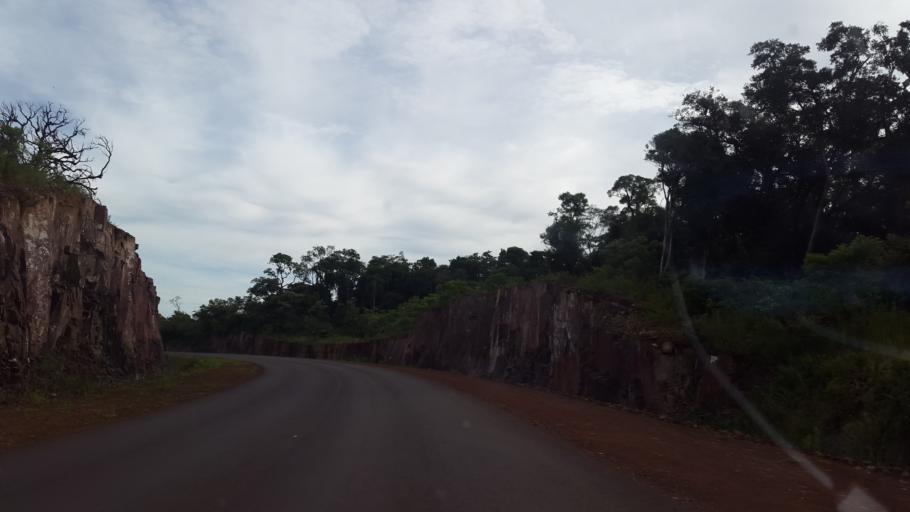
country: AR
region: Misiones
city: Bernardo de Irigoyen
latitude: -26.4522
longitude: -53.8561
